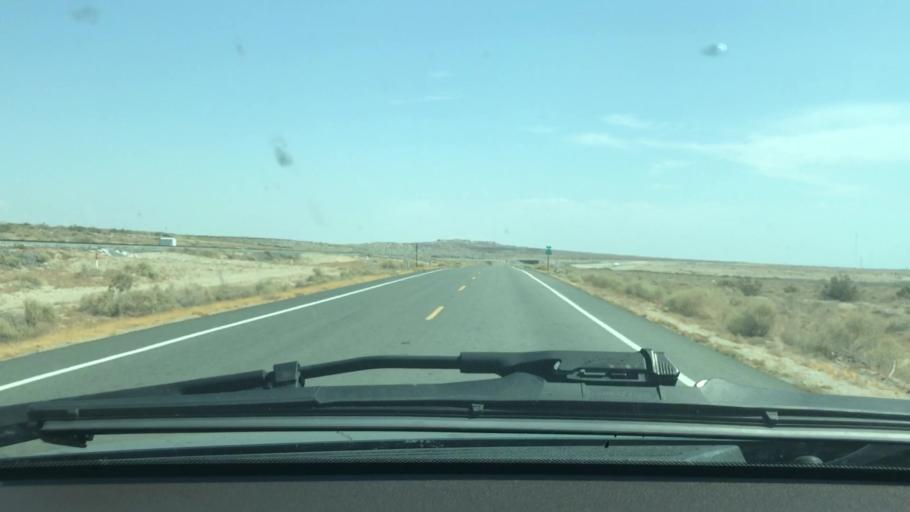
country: US
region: California
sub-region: Imperial County
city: Salton City
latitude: 33.4524
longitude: -115.8519
